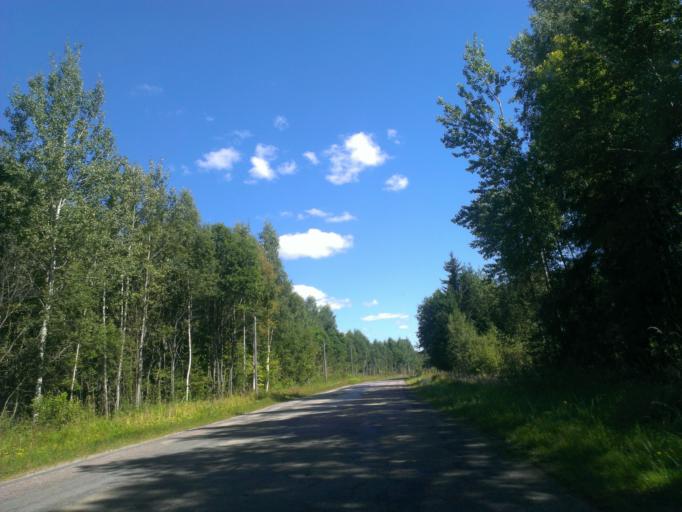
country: LV
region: Malpils
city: Malpils
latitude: 57.0197
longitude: 24.9094
